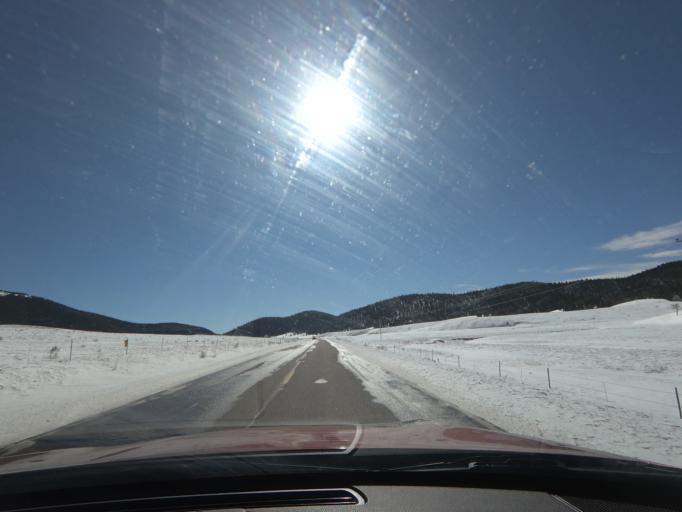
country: US
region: Colorado
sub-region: Teller County
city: Cripple Creek
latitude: 38.7674
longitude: -105.1178
